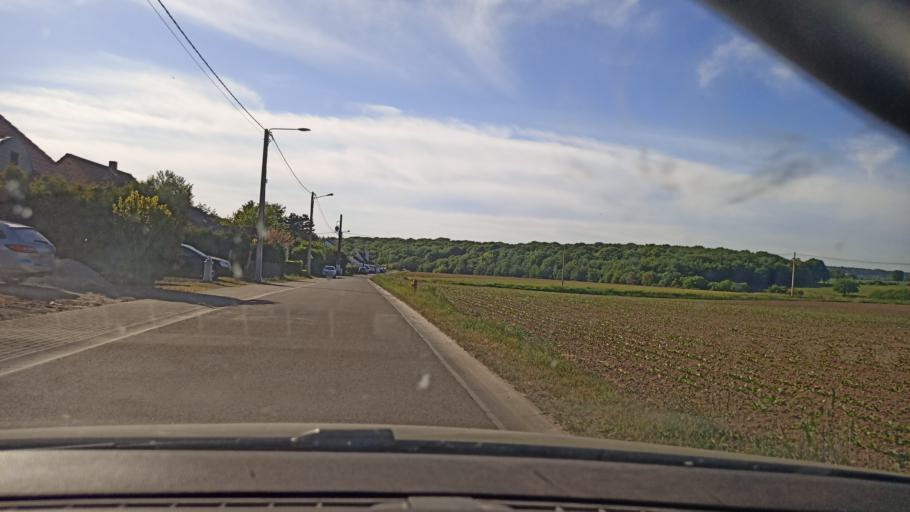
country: BE
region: Wallonia
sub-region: Province du Hainaut
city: Lobbes
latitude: 50.3291
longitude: 4.2598
